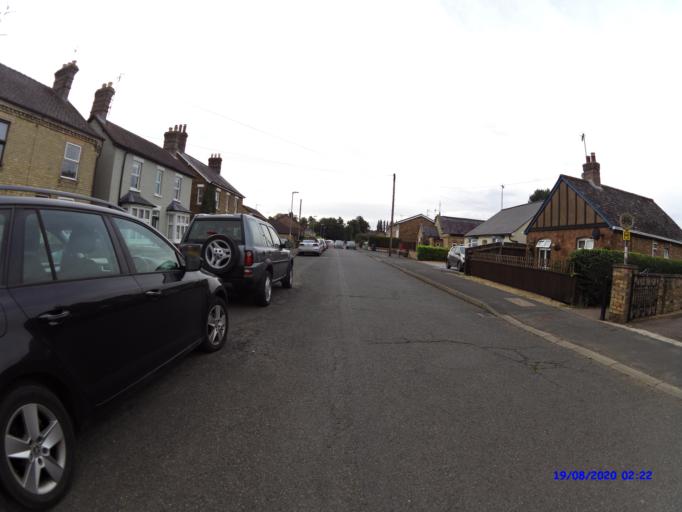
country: GB
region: England
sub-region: Cambridgeshire
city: Ramsey
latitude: 52.4517
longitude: -0.1070
